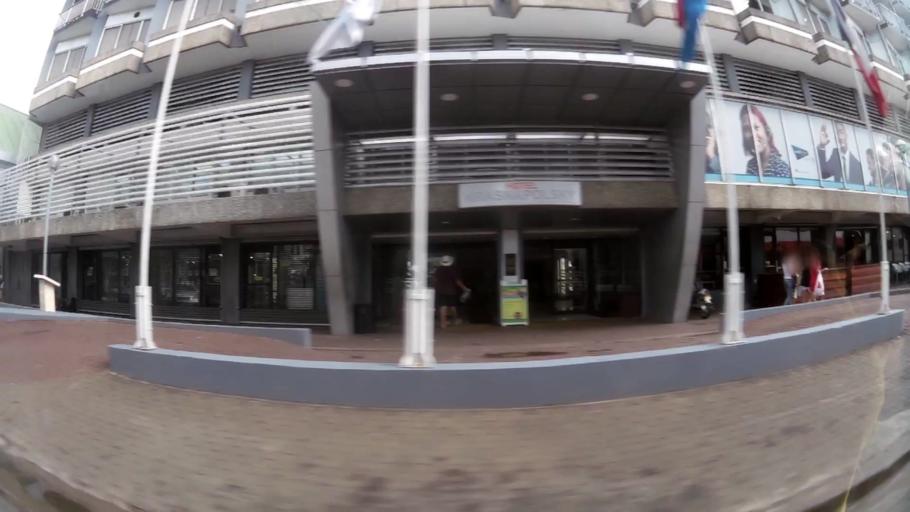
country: SR
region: Paramaribo
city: Paramaribo
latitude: 5.8263
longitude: -55.1603
